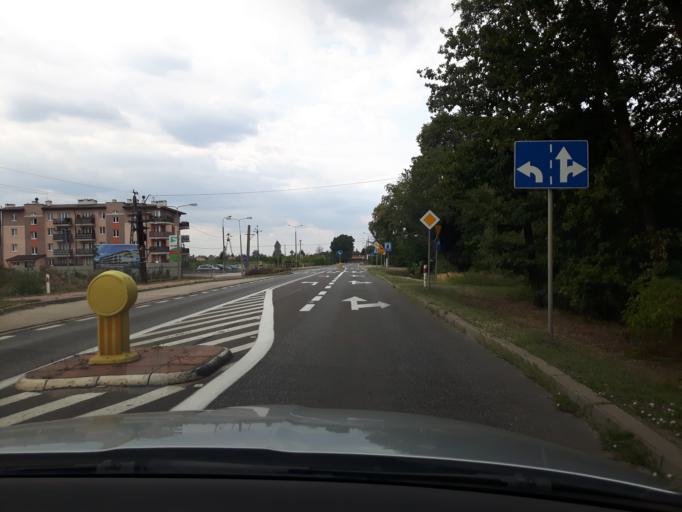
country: PL
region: Masovian Voivodeship
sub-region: Powiat legionowski
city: Wieliszew
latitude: 52.4478
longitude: 20.9786
